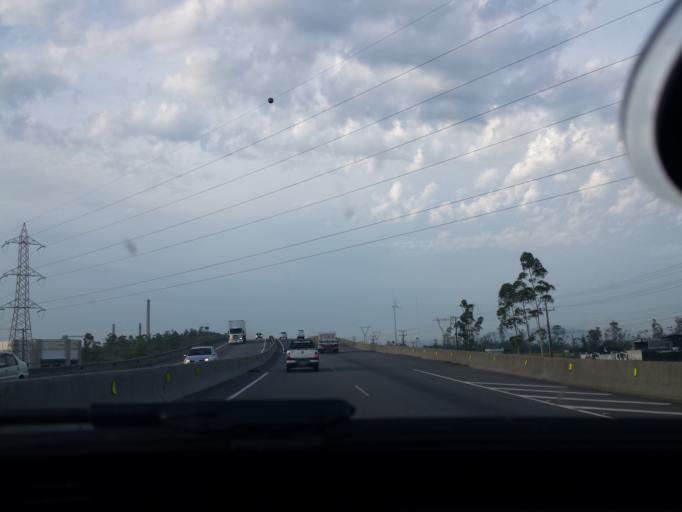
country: BR
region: Santa Catarina
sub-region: Tubarao
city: Tubarao
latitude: -28.4380
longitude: -48.9613
